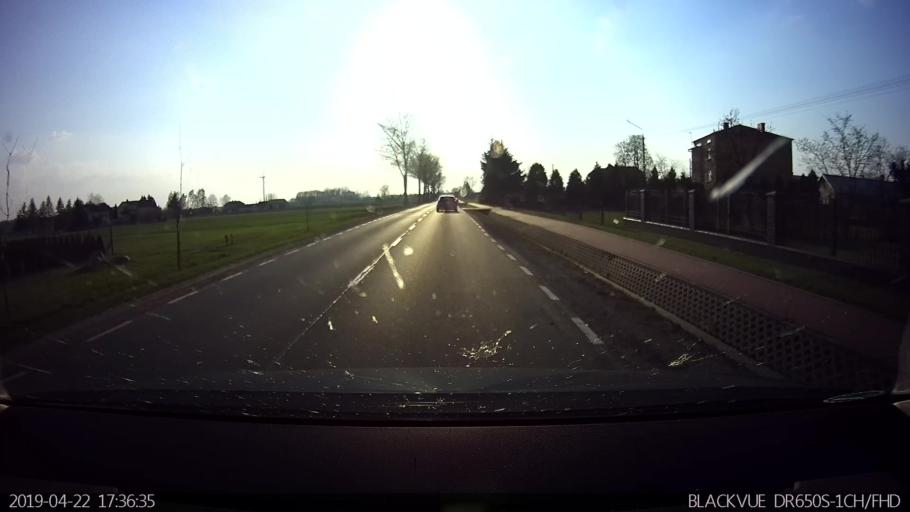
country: PL
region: Masovian Voivodeship
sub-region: Powiat sokolowski
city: Sokolow Podlaski
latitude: 52.4075
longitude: 22.1875
